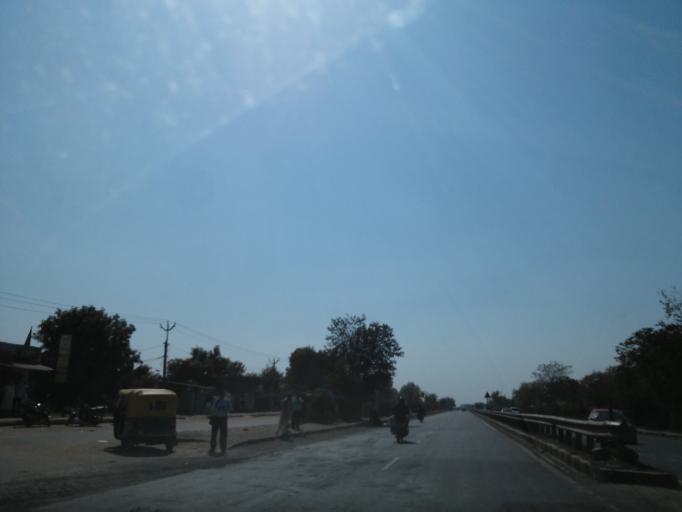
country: IN
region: Gujarat
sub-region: Gandhinagar
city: Chhala
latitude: 23.3111
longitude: 72.7747
